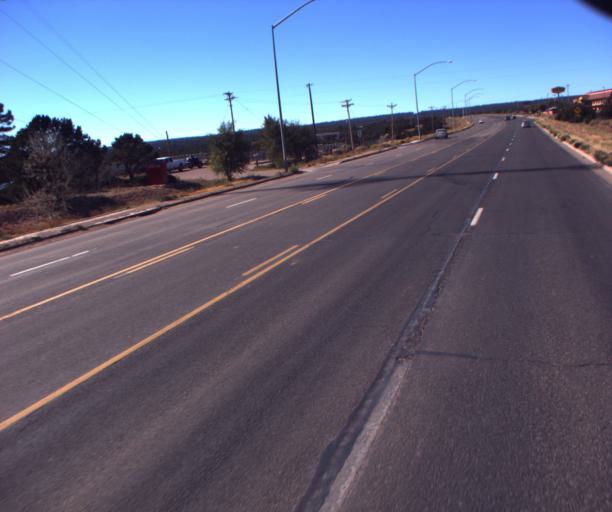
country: US
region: Arizona
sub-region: Apache County
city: Saint Michaels
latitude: 35.6572
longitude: -109.1103
